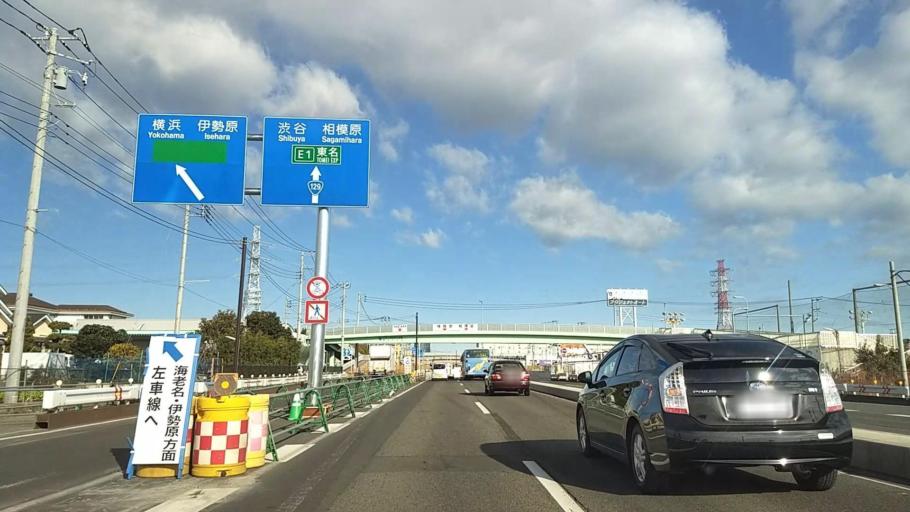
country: JP
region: Kanagawa
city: Atsugi
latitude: 35.4020
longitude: 139.3616
